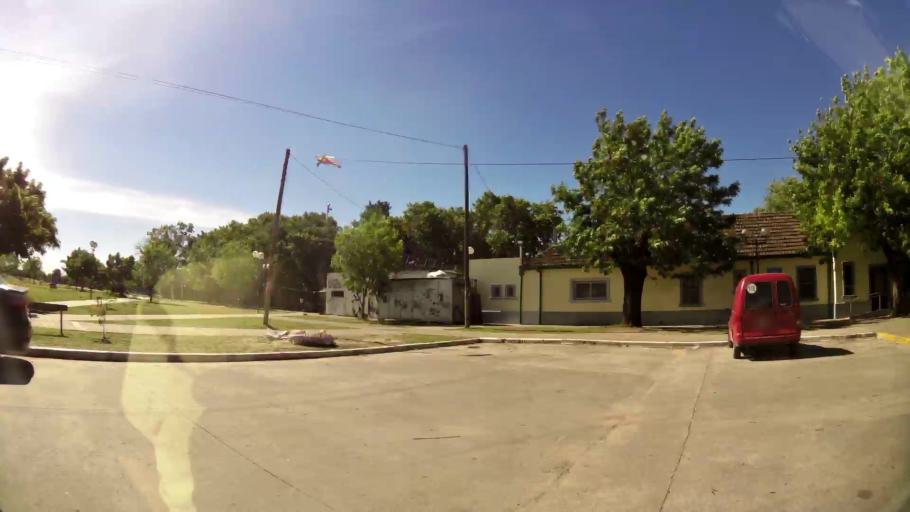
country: AR
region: Buenos Aires
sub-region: Partido de Almirante Brown
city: Adrogue
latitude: -34.7971
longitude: -58.3592
